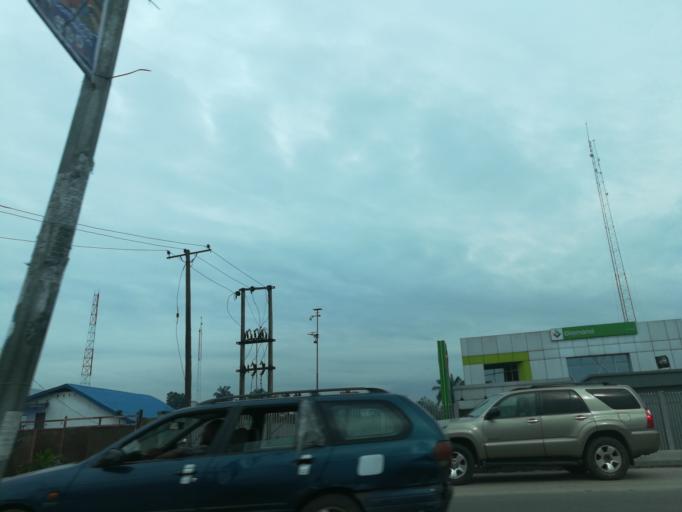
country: NG
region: Rivers
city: Port Harcourt
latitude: 4.8088
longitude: 7.0130
